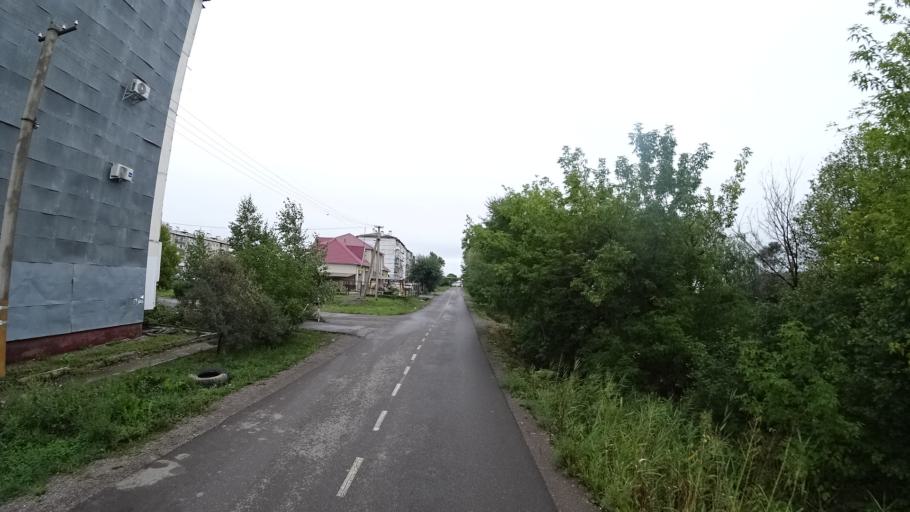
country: RU
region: Primorskiy
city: Monastyrishche
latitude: 44.2031
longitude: 132.4448
